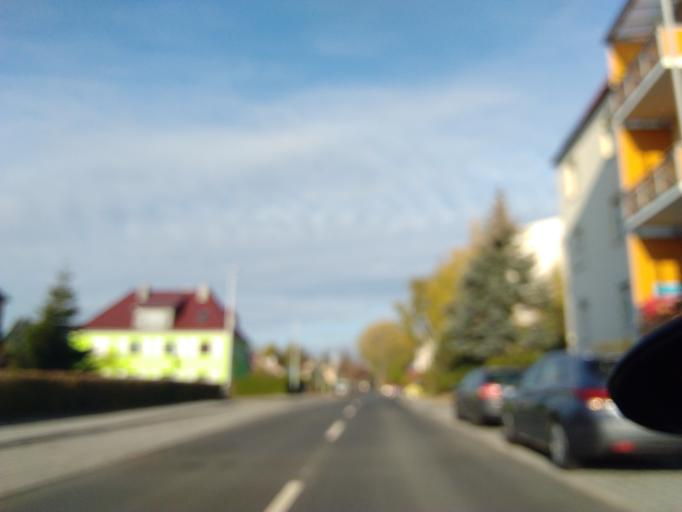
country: DE
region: Saxony
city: Meissen
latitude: 51.1779
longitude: 13.4944
